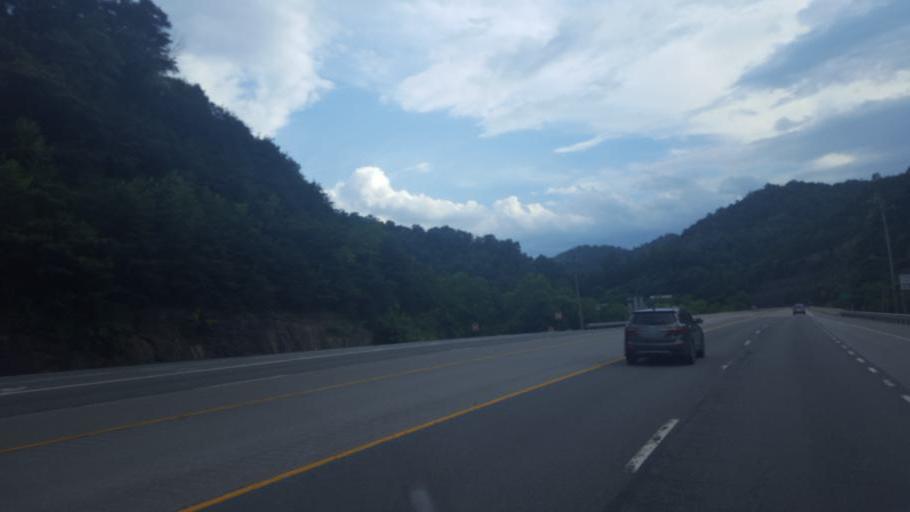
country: US
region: Kentucky
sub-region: Pike County
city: Pikeville
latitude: 37.4380
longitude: -82.5100
